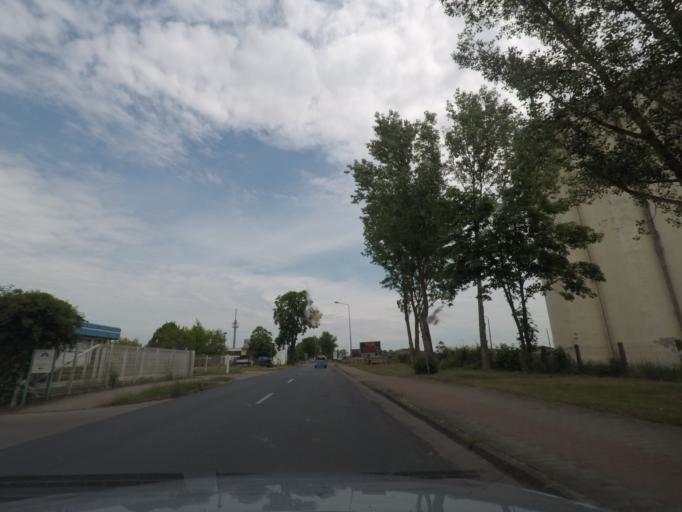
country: DE
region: Brandenburg
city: Prenzlau
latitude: 53.3280
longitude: 13.8873
